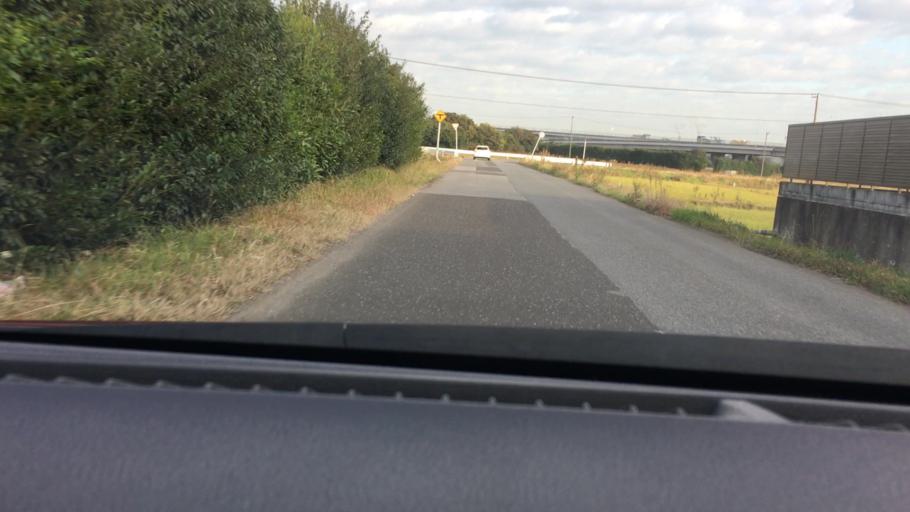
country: JP
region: Chiba
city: Kisarazu
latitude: 35.4064
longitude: 139.9601
